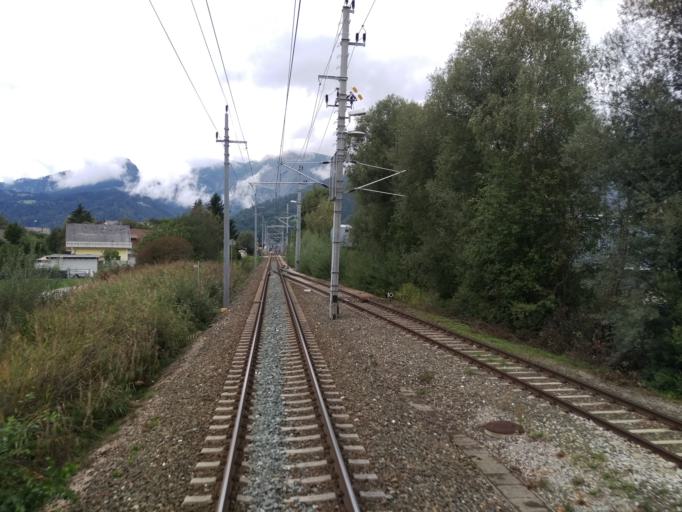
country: AT
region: Styria
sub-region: Politischer Bezirk Liezen
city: Liezen
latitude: 47.5588
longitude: 14.2497
